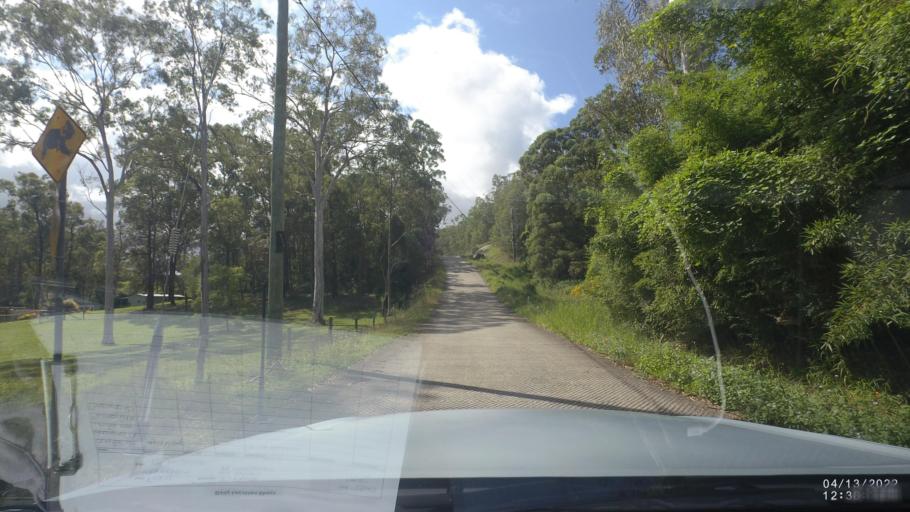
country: AU
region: Queensland
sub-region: Logan
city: Windaroo
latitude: -27.7955
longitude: 153.1490
